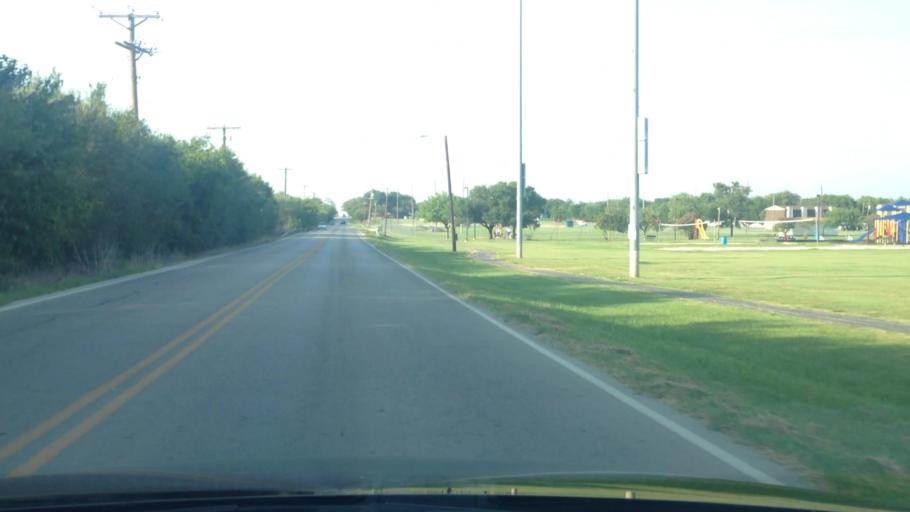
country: US
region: Texas
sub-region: Tarrant County
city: Everman
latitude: 32.6333
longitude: -97.2888
